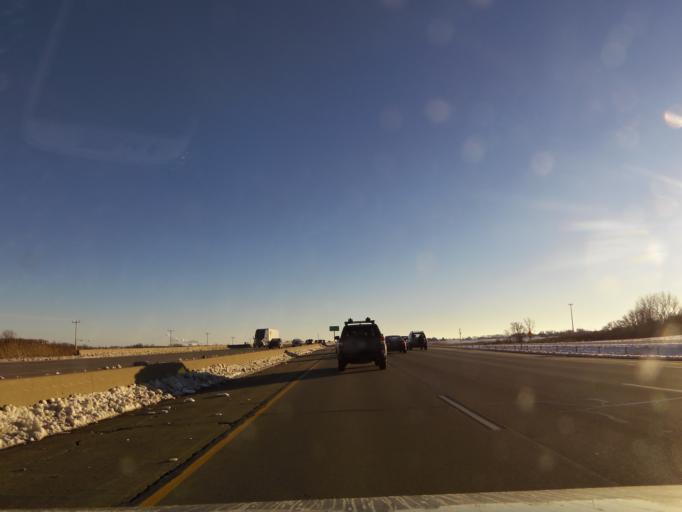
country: US
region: Wisconsin
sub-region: Kenosha County
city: Somers
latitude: 42.6579
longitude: -87.9528
